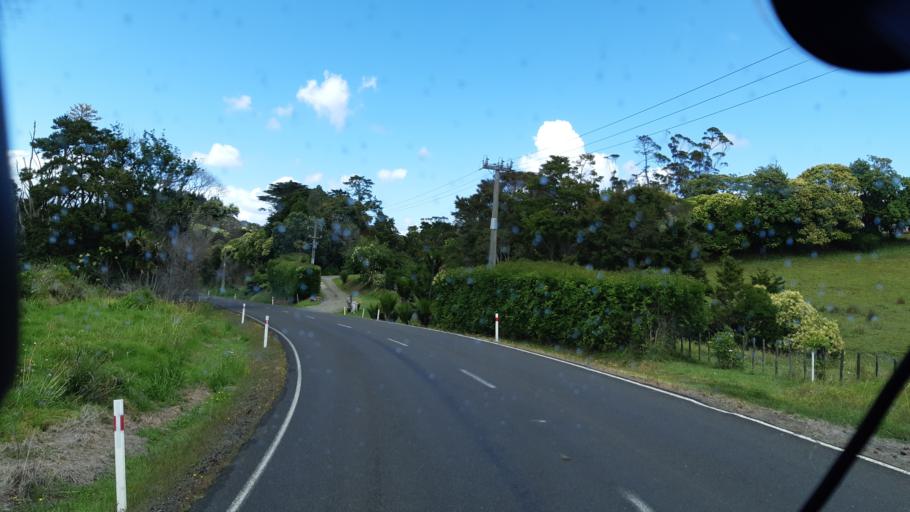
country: NZ
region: Northland
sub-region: Far North District
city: Taipa
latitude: -35.2692
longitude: 173.5234
